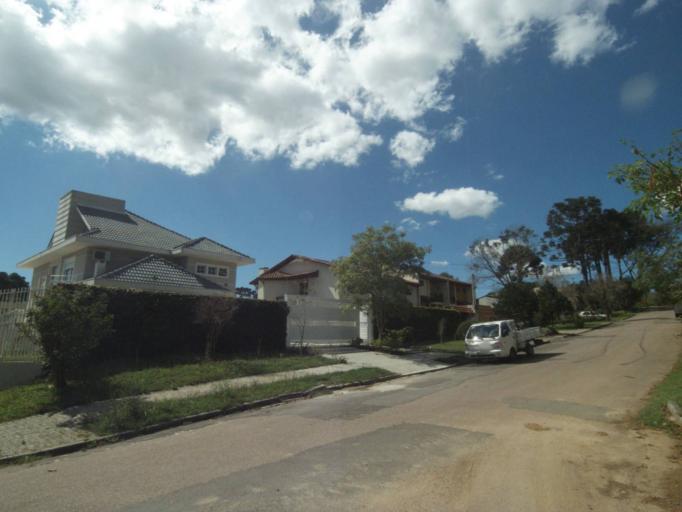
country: BR
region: Parana
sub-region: Curitiba
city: Curitiba
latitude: -25.3818
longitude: -49.2435
